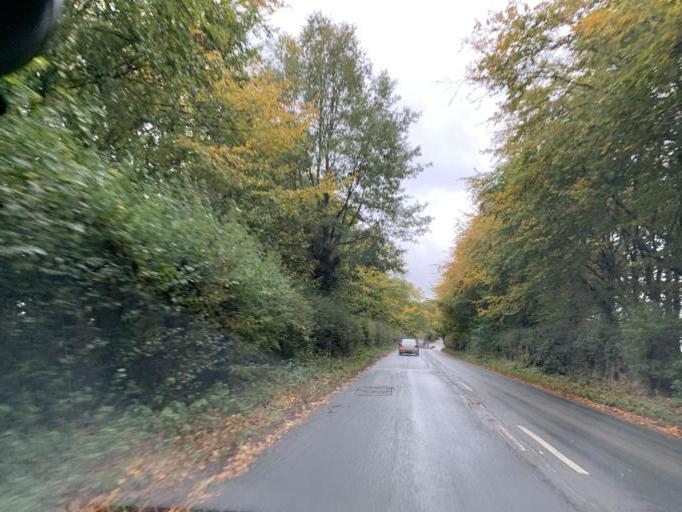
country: GB
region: England
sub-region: Wiltshire
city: Woodford
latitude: 51.0973
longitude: -1.8421
